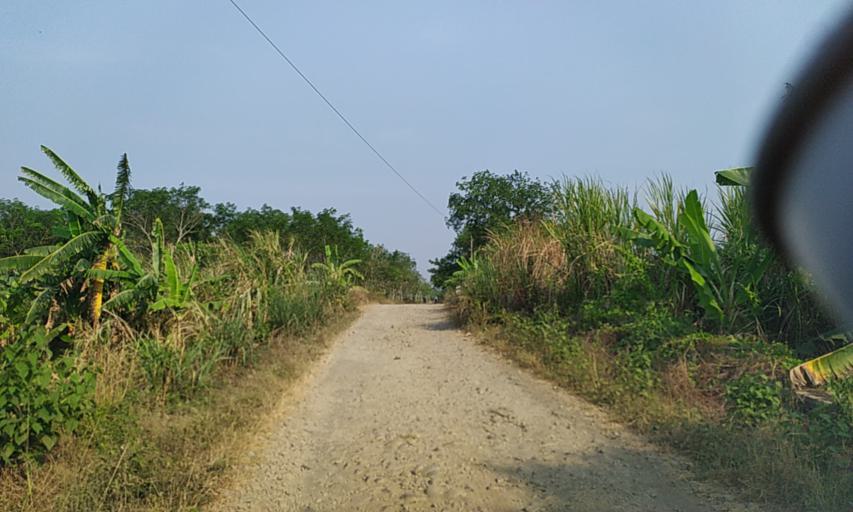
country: ID
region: Central Java
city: Padangsari
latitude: -7.3576
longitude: 108.7622
